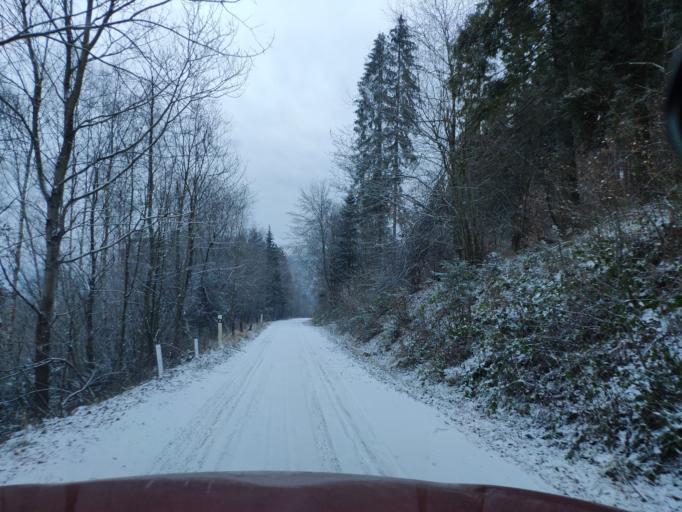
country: SK
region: Kosicky
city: Spisska Nova Ves
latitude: 48.8152
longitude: 20.5517
